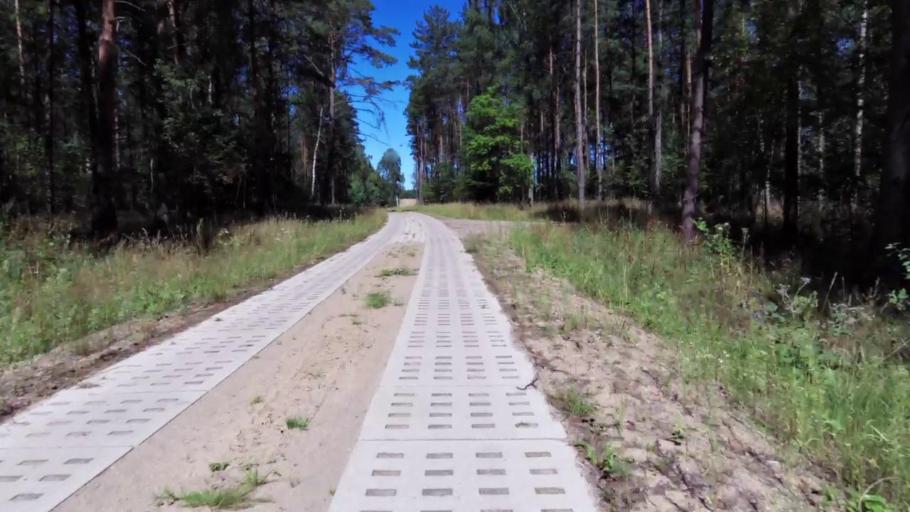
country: PL
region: West Pomeranian Voivodeship
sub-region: Powiat szczecinecki
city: Szczecinek
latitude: 53.6274
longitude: 16.6611
